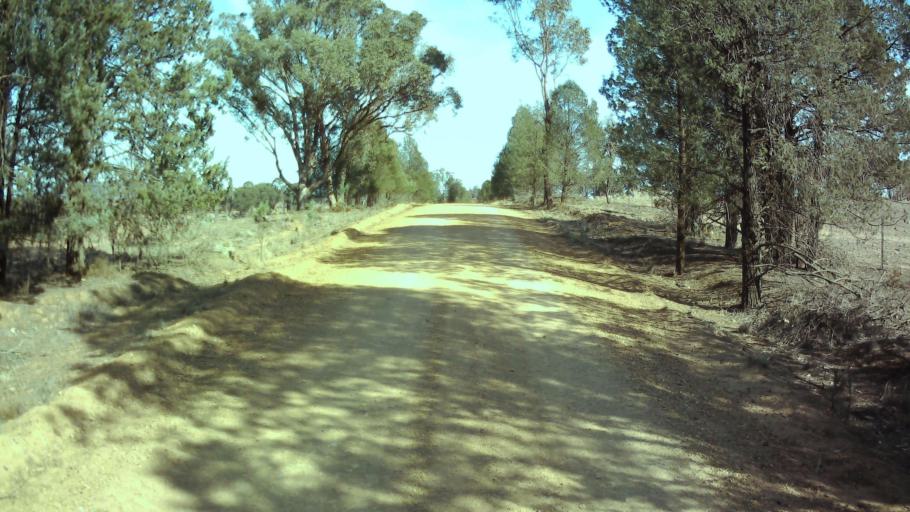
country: AU
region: New South Wales
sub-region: Weddin
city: Grenfell
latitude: -33.7560
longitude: 148.0258
